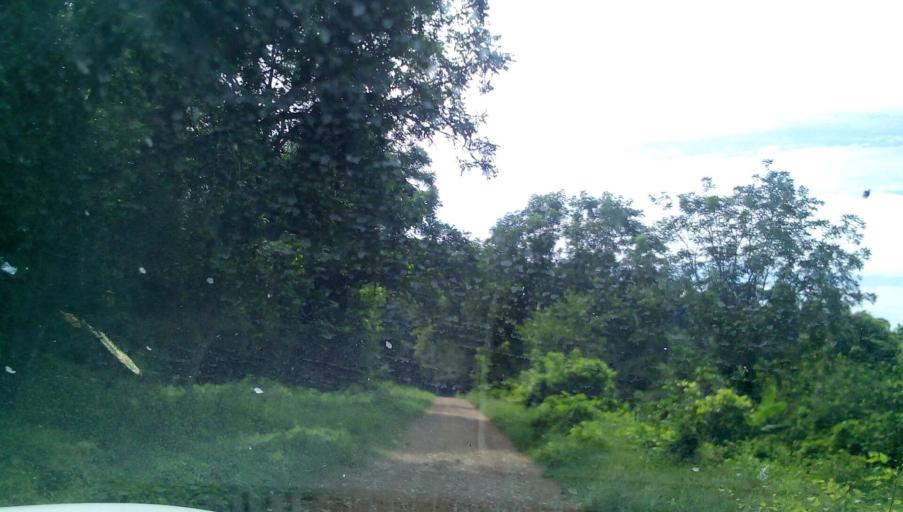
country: MX
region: Veracruz
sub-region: Alamo Temapache
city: Vegas de la Soledad y Soledad Dos
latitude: 20.8961
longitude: -97.9458
